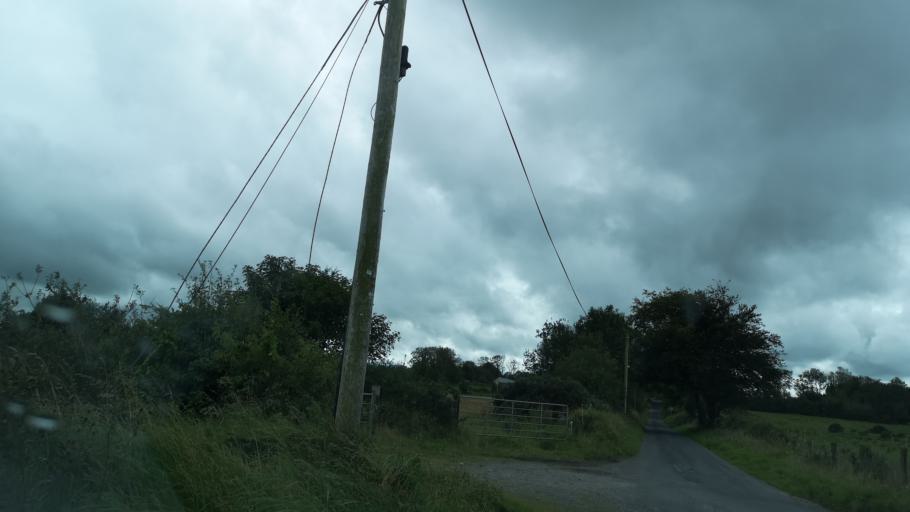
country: IE
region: Connaught
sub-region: County Galway
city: Loughrea
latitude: 53.2990
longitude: -8.5884
